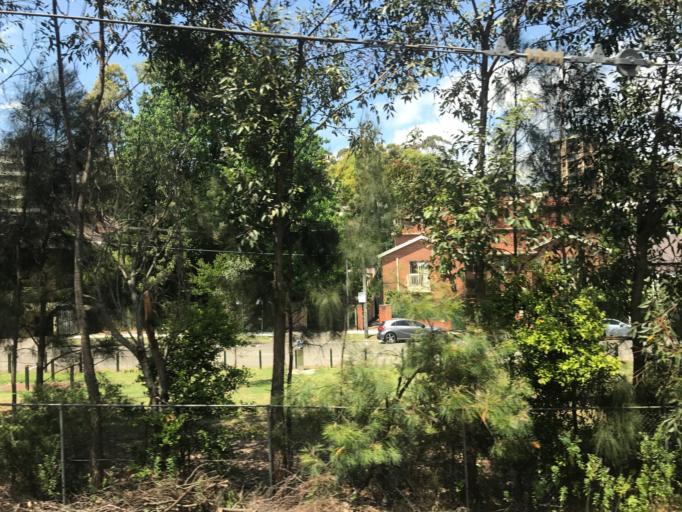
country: AU
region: New South Wales
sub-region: North Sydney
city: St Leonards
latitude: -33.8274
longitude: 151.1957
